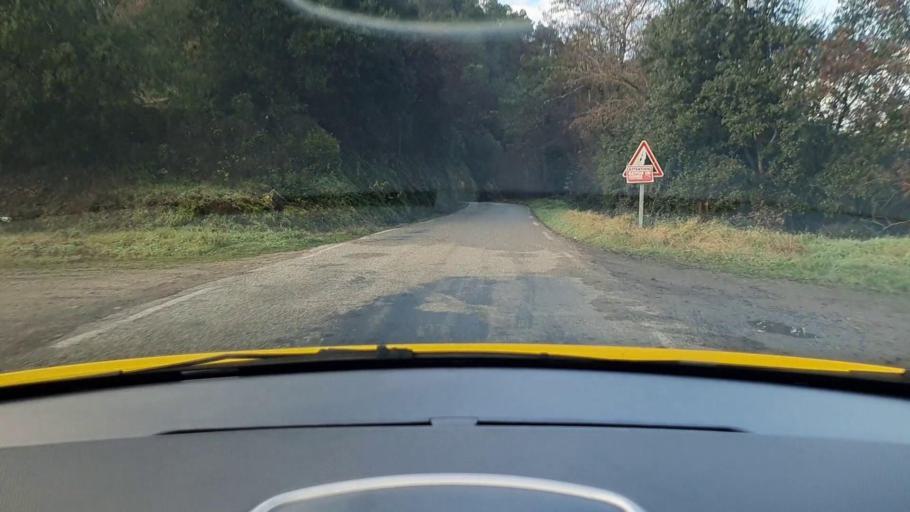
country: FR
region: Languedoc-Roussillon
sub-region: Departement du Gard
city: Branoux-les-Taillades
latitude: 44.2980
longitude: 3.9977
